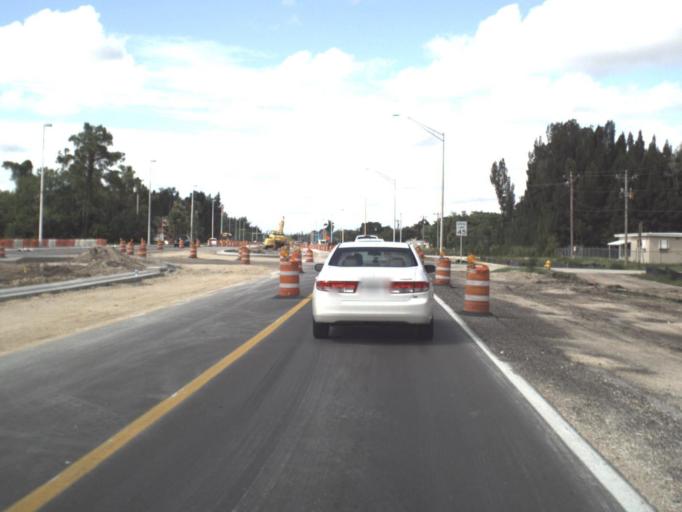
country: US
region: Florida
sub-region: Lee County
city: Palmona Park
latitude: 26.6995
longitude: -81.8912
